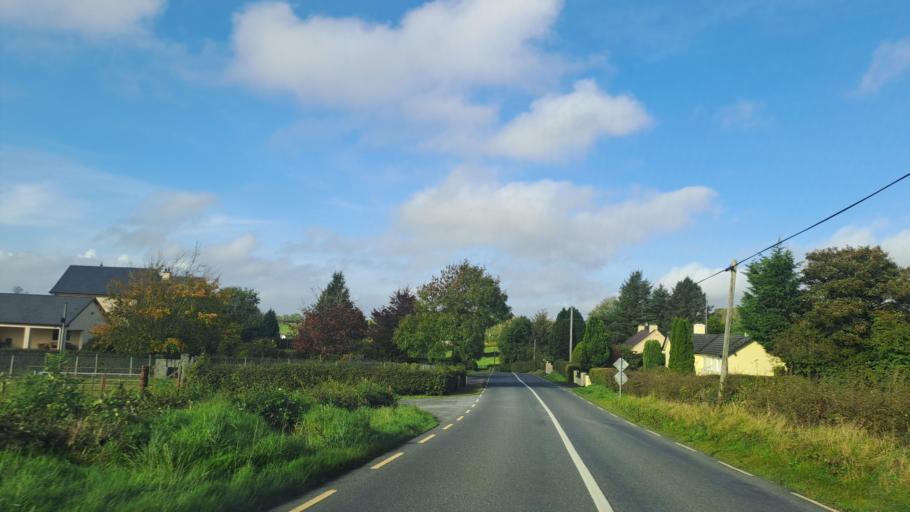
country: IE
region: Ulster
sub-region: An Cabhan
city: Cootehill
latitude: 54.0594
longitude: -7.0307
